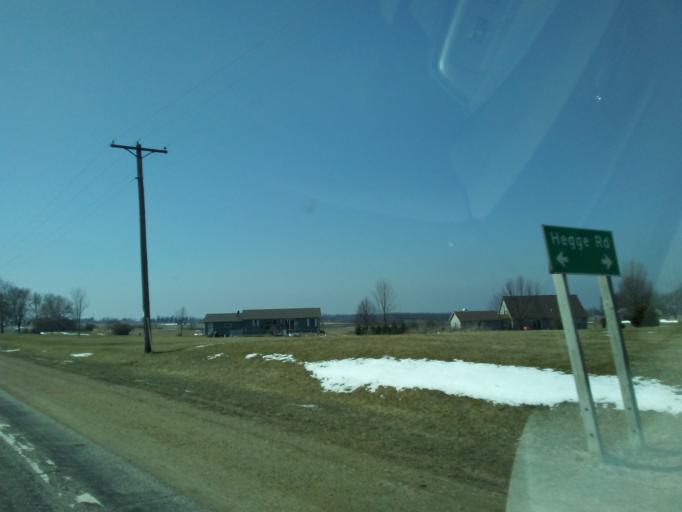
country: US
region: Wisconsin
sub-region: Vernon County
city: Westby
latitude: 43.6659
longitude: -90.8881
